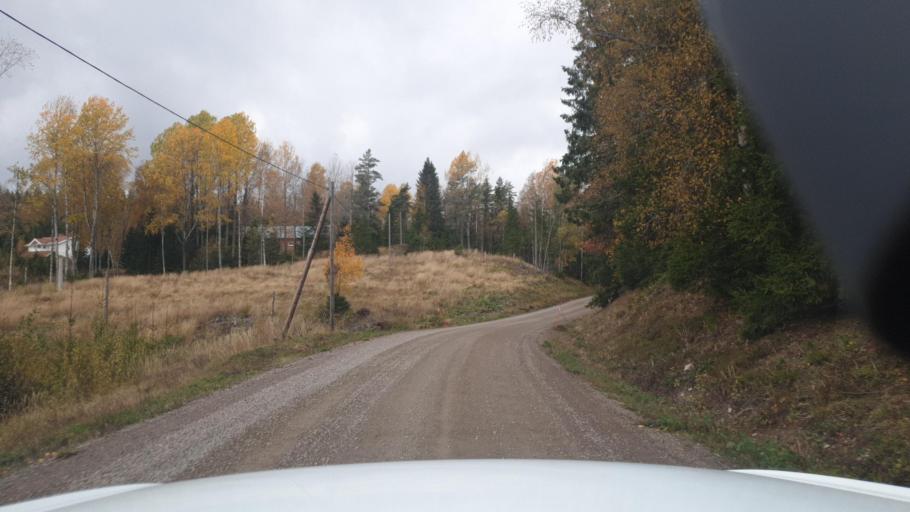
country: SE
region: Vaermland
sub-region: Sunne Kommun
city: Sunne
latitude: 59.8219
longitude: 12.8783
